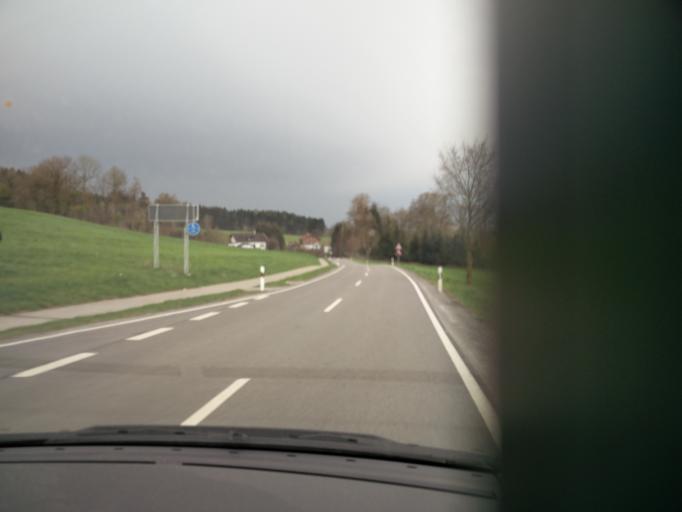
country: DE
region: Bavaria
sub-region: Upper Bavaria
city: Halfing
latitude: 47.9575
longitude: 12.2899
